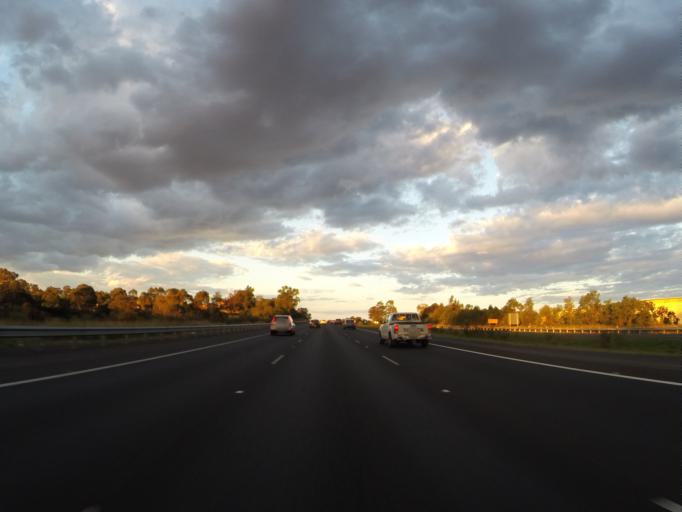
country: AU
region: New South Wales
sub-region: Campbelltown Municipality
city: Campbelltown
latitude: -34.0545
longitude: 150.8038
